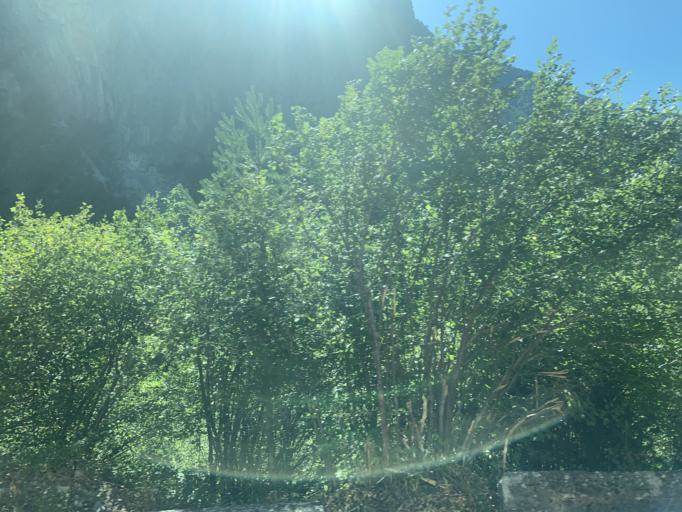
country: ES
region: Aragon
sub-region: Provincia de Huesca
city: Broto
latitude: 42.6454
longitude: -0.1067
